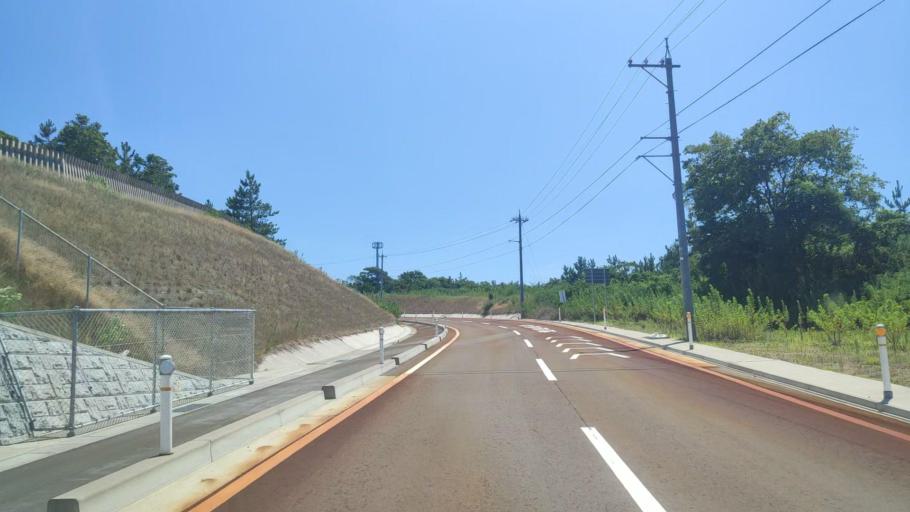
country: JP
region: Ishikawa
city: Kanazawa-shi
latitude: 36.6750
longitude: 136.6538
